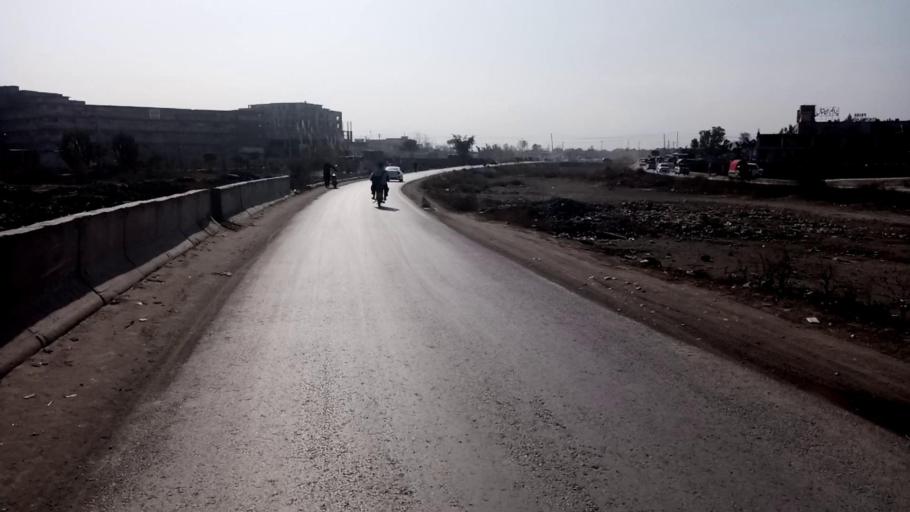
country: PK
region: Khyber Pakhtunkhwa
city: Peshawar
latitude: 34.0371
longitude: 71.5329
